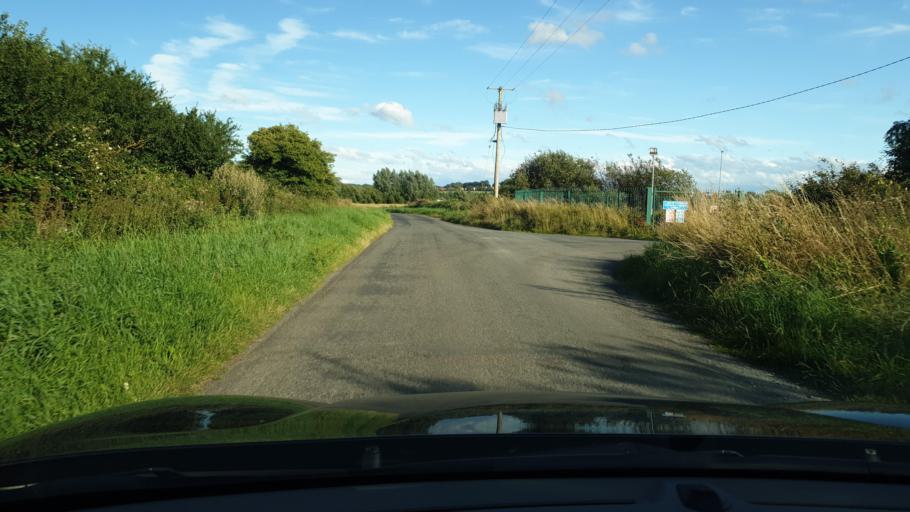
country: IE
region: Leinster
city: Balrothery
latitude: 53.5786
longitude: -6.2227
